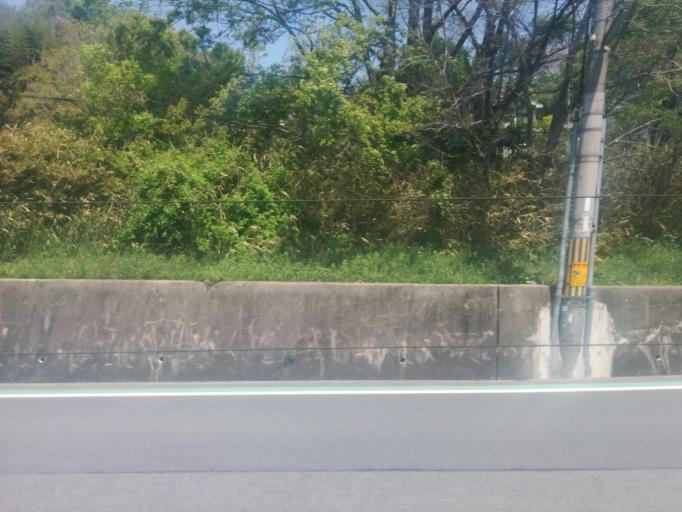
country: JP
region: Osaka
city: Kashihara
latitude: 34.5527
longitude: 135.6633
